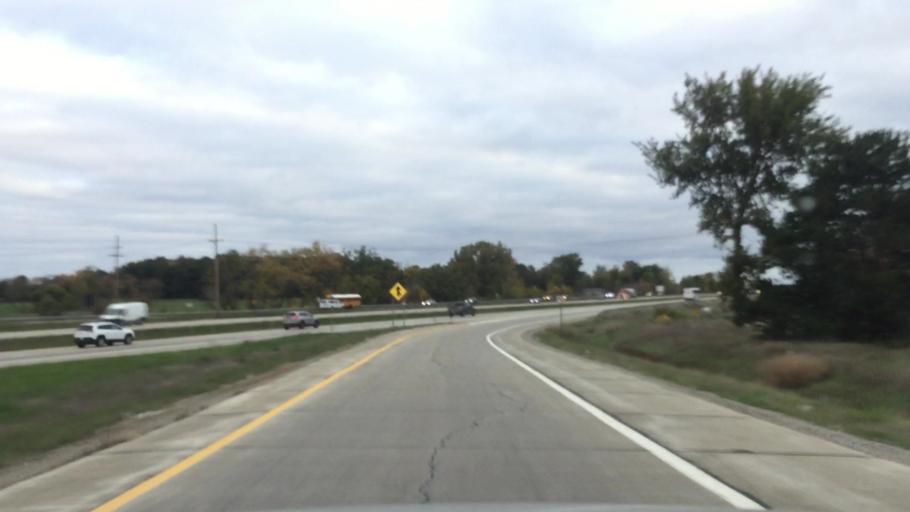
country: US
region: Michigan
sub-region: Genesee County
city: Fenton
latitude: 42.6781
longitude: -83.7593
